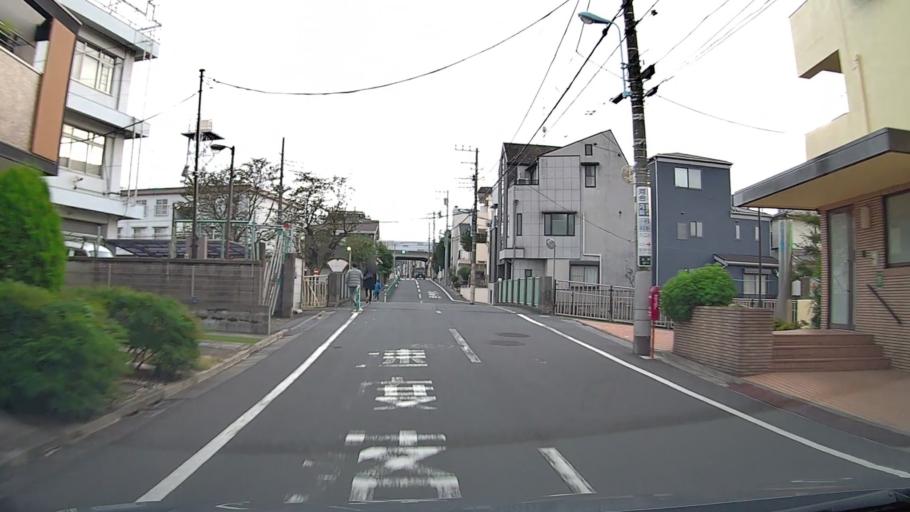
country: JP
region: Tokyo
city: Musashino
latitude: 35.7053
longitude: 139.6100
